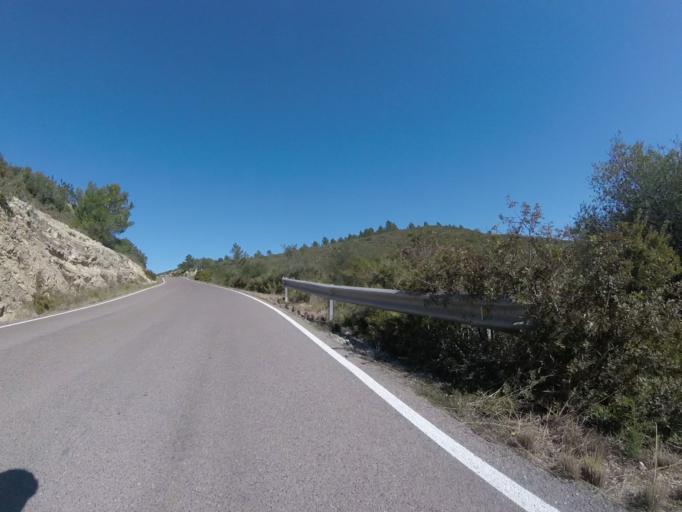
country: ES
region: Valencia
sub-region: Provincia de Castello
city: Santa Magdalena de Pulpis
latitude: 40.3853
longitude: 0.2537
